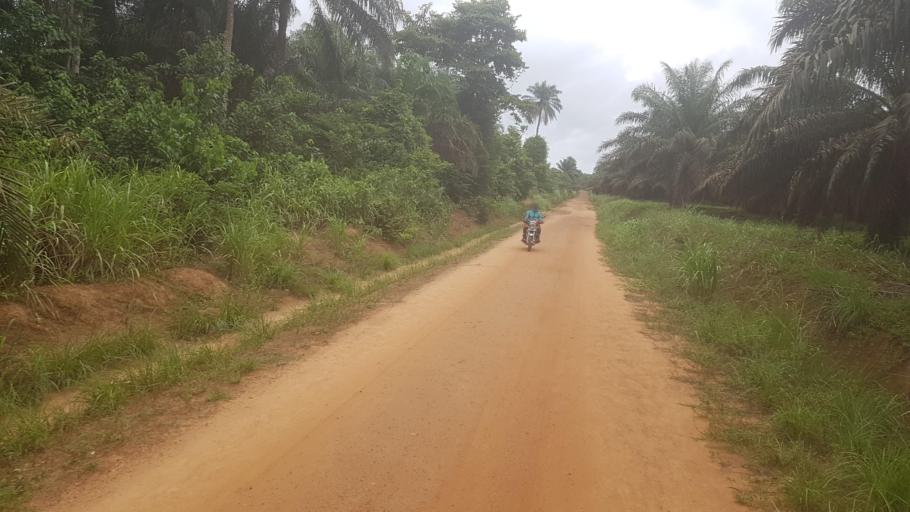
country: SL
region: Southern Province
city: Sumbuya
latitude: 7.5422
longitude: -12.1691
